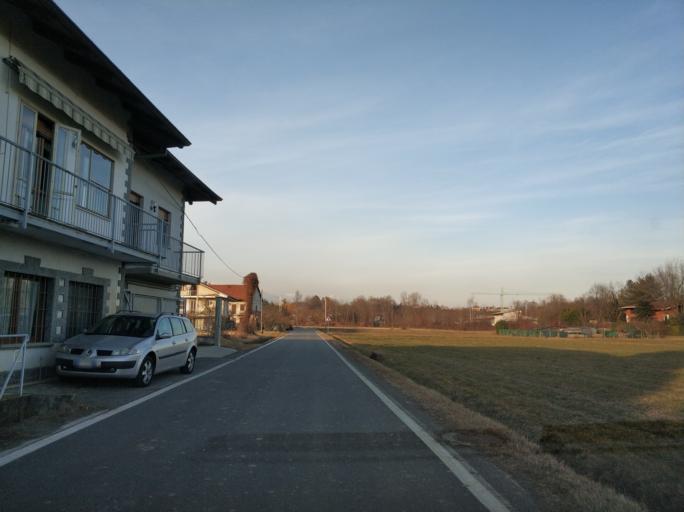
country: IT
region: Piedmont
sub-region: Provincia di Torino
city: San Francesco al Campo
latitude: 45.2224
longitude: 7.6455
